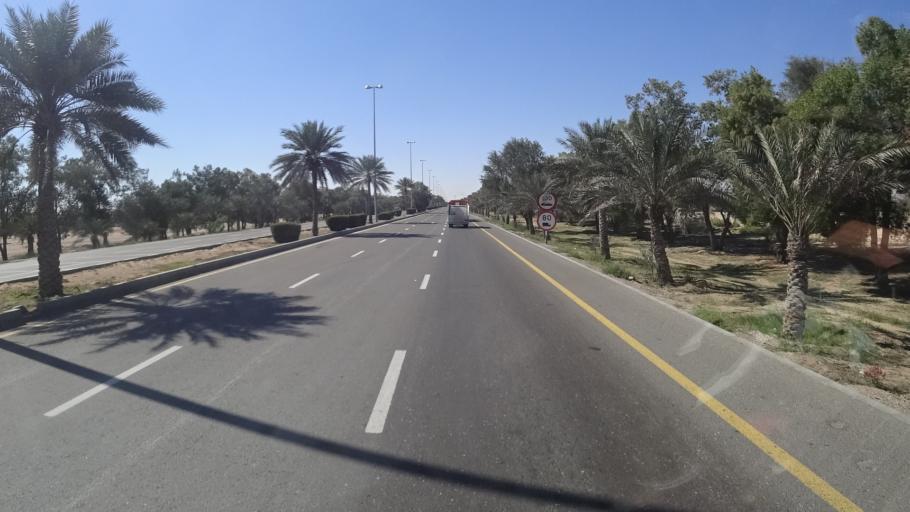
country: AE
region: Abu Dhabi
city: Al Ain
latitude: 24.1015
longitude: 55.6935
